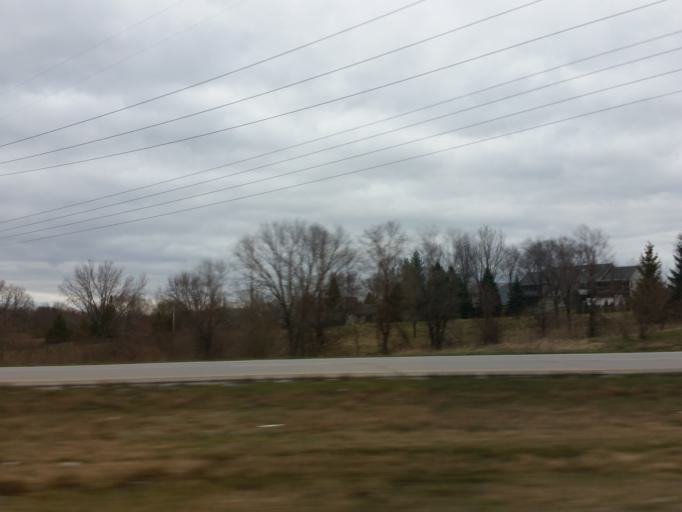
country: US
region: Iowa
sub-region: Johnson County
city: University Heights
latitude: 41.6403
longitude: -91.5745
